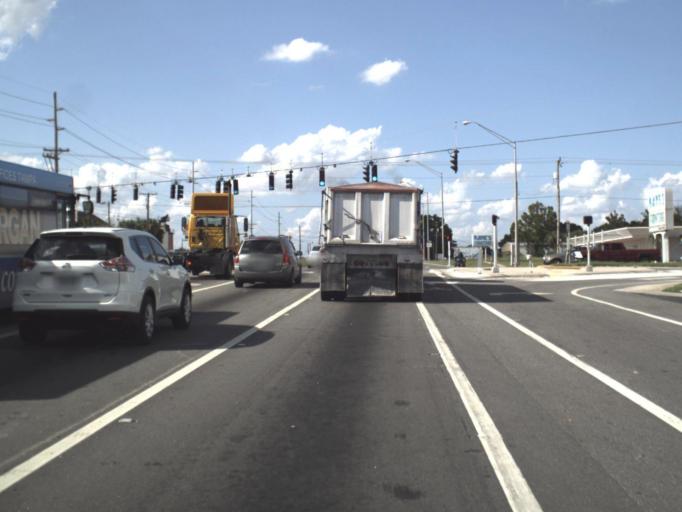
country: US
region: Florida
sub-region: Hillsborough County
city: East Lake-Orient Park
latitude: 27.9956
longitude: -82.3934
